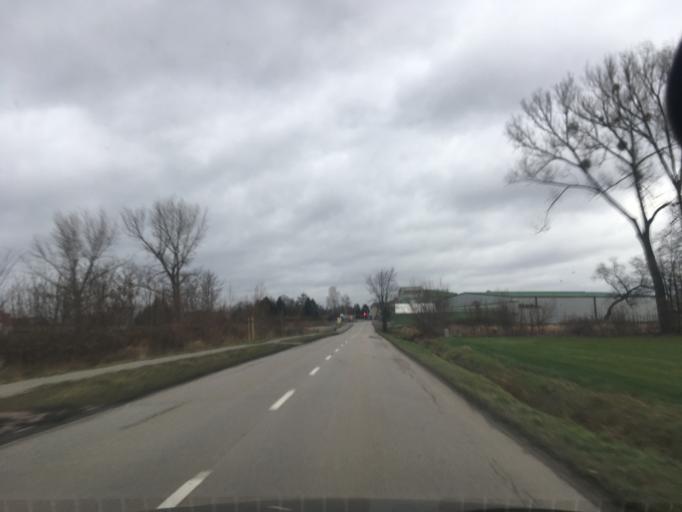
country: PL
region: Masovian Voivodeship
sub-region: Powiat pruszkowski
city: Rybie
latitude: 52.1330
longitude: 20.9724
